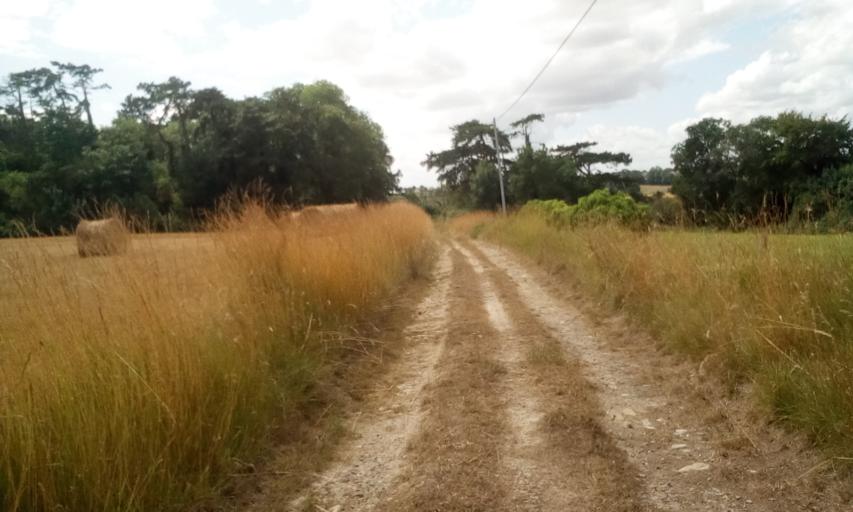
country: FR
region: Lower Normandy
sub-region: Departement du Calvados
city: Creully
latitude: 49.2888
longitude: -0.5191
